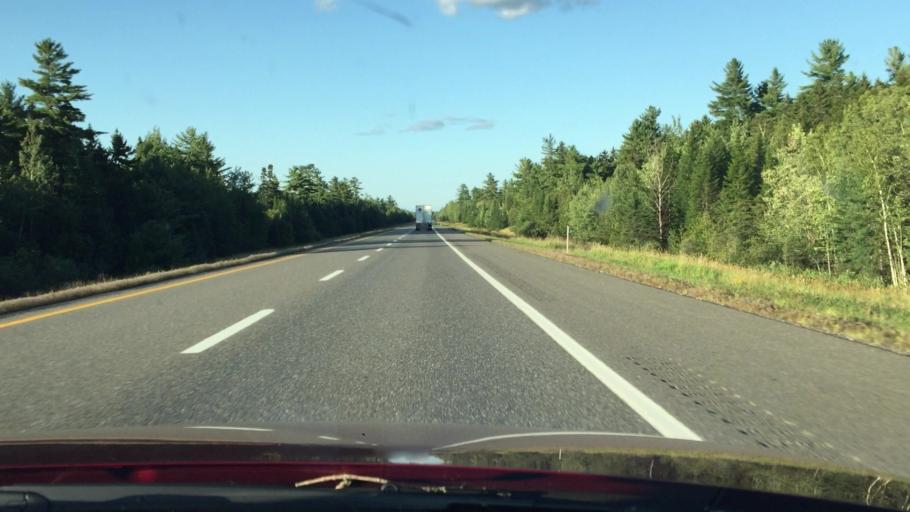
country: US
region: Maine
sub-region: Penobscot County
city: Patten
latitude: 46.0648
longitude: -68.2288
